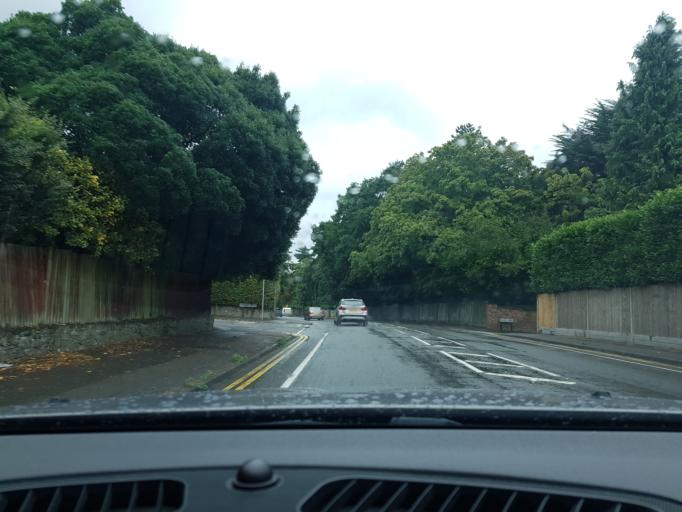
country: GB
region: England
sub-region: Surrey
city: Guildford
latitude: 51.2402
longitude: -0.5510
